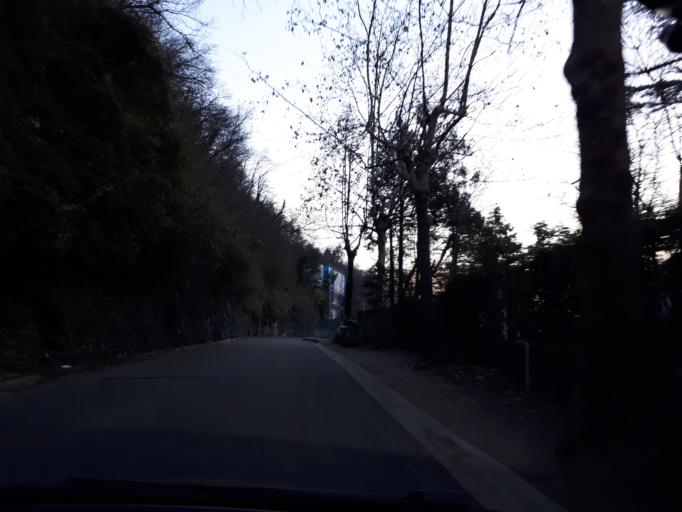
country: IT
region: Lombardy
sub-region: Provincia di Como
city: Nesso
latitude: 45.9040
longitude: 9.1551
